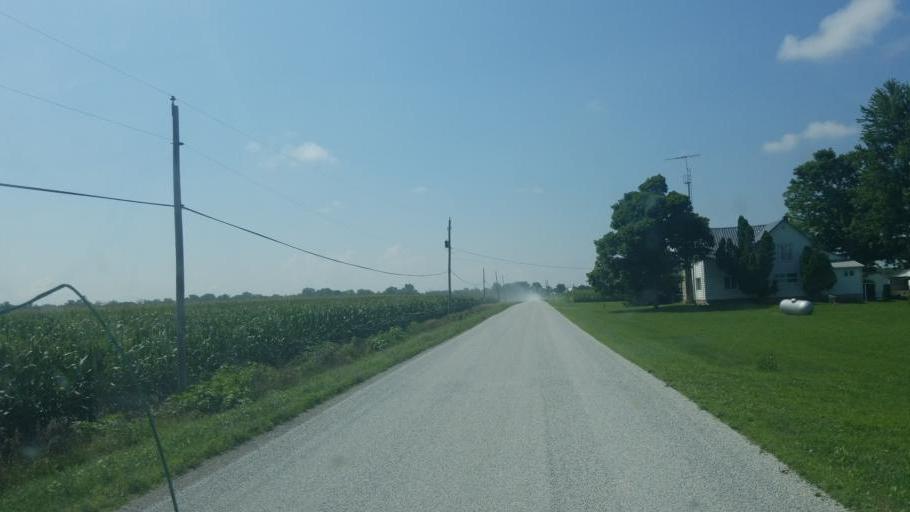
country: US
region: Ohio
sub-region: Hardin County
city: Ada
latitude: 40.6915
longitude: -83.7305
